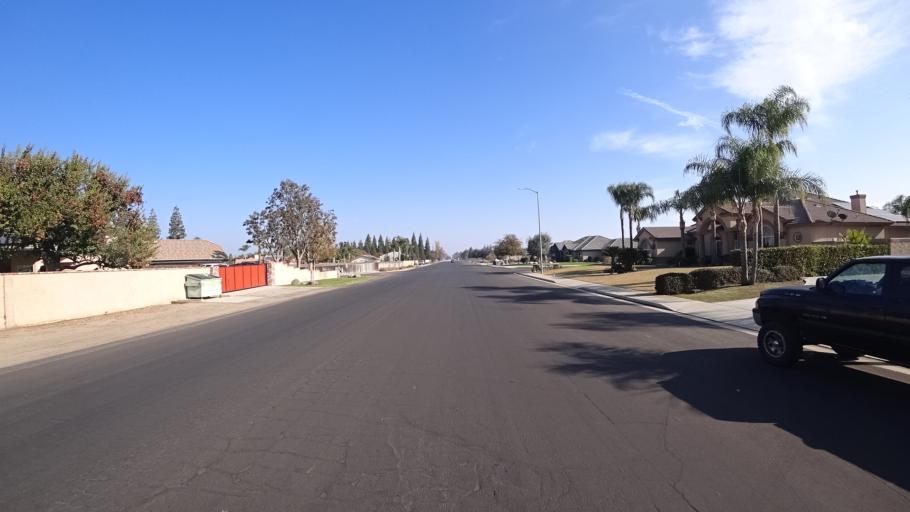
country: US
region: California
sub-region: Kern County
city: Rosedale
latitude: 35.3617
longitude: -119.1752
